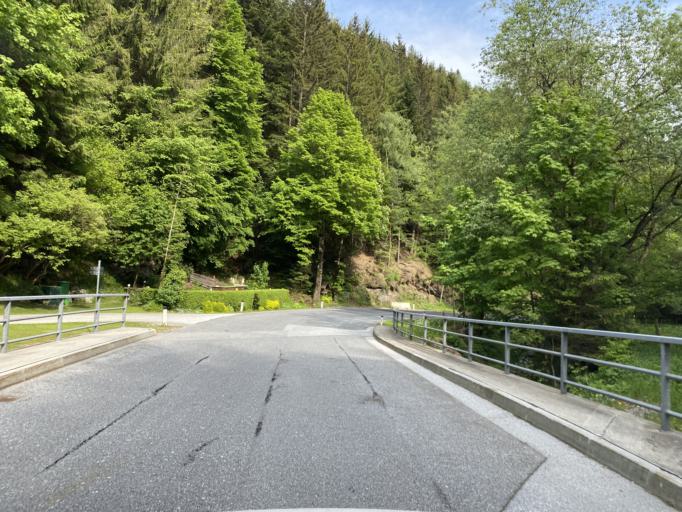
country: AT
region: Styria
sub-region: Politischer Bezirk Weiz
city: Koglhof
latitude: 47.3112
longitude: 15.6562
